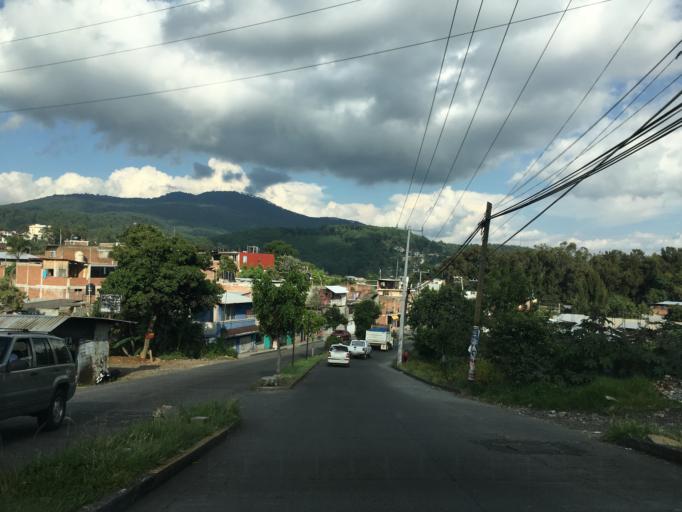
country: MX
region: Michoacan
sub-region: Uruapan
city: Uruapan
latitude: 19.4307
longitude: -102.0776
